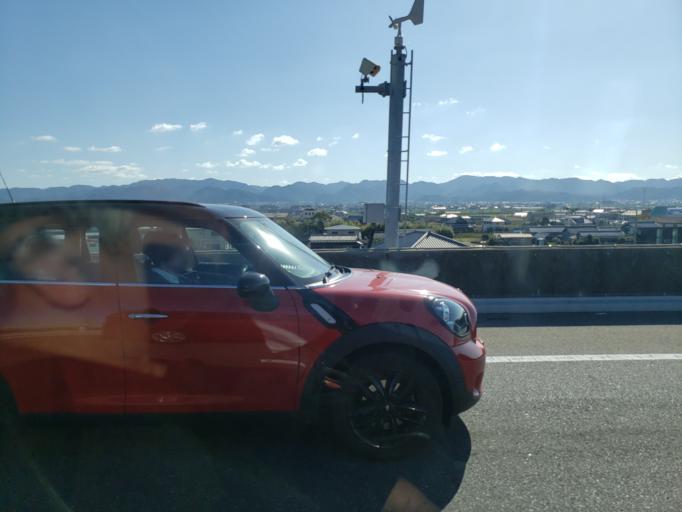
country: JP
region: Hyogo
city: Fukura
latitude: 34.3062
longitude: 134.7440
